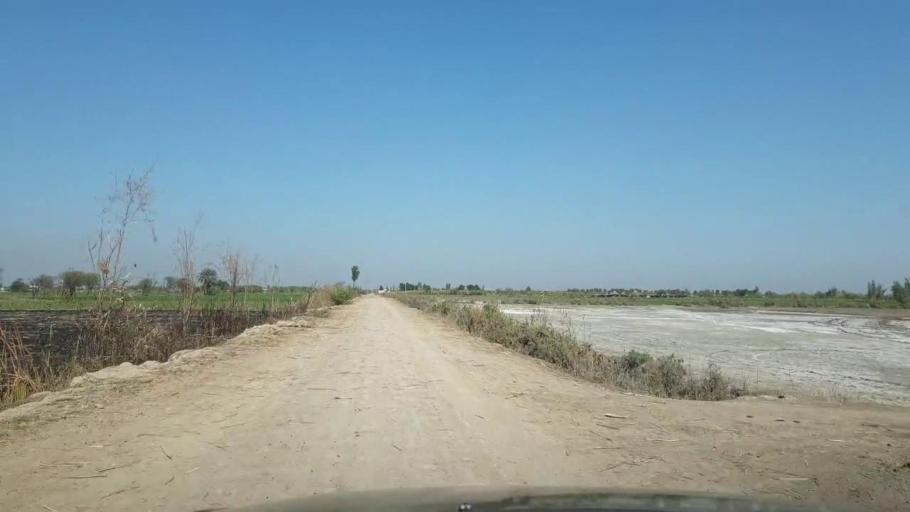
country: PK
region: Sindh
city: Mirpur Khas
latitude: 25.5938
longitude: 69.0555
